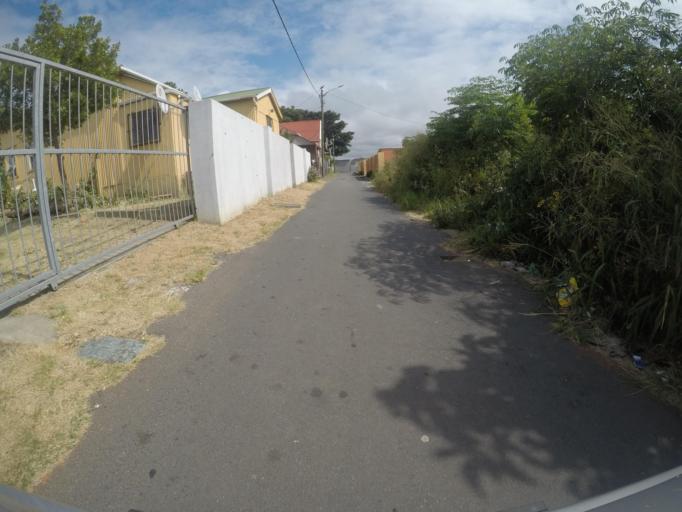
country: ZA
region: Eastern Cape
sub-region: Buffalo City Metropolitan Municipality
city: East London
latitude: -32.9983
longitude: 27.9079
